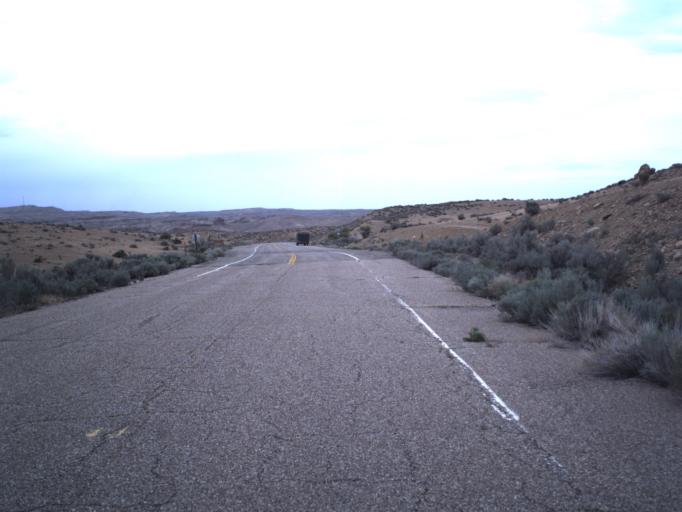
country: US
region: Colorado
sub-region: Rio Blanco County
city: Rangely
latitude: 39.9579
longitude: -109.1637
